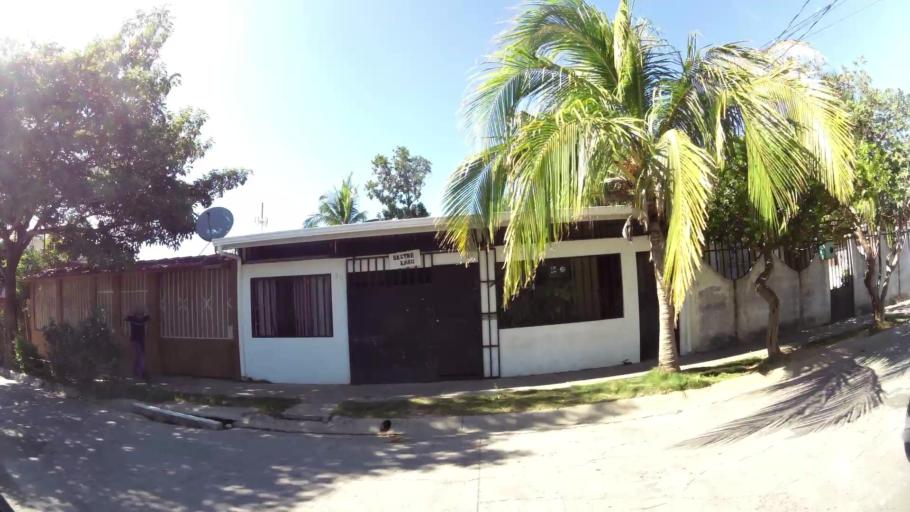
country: CR
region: Guanacaste
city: Liberia
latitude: 10.6376
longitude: -85.4346
